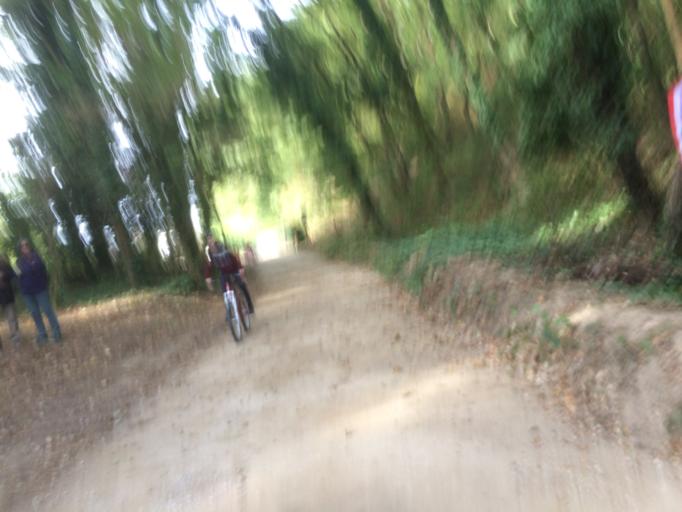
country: FR
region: Ile-de-France
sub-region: Departement des Yvelines
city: Bonnelles
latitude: 48.6255
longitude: 2.0229
